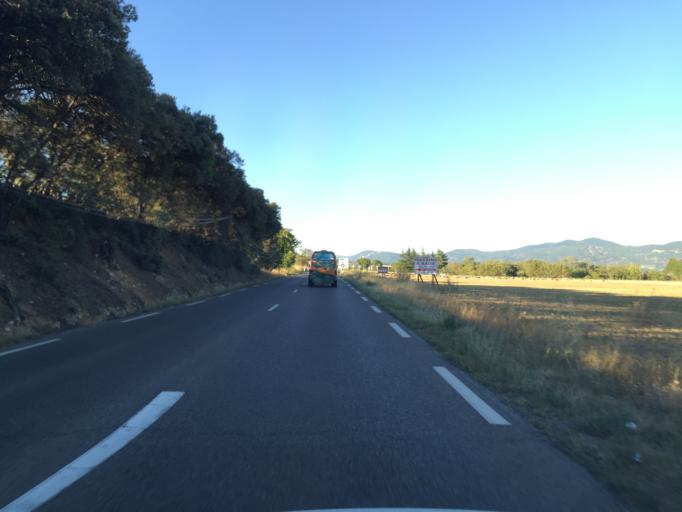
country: FR
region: Provence-Alpes-Cote d'Azur
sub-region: Departement des Alpes-de-Haute-Provence
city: Les Mees
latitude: 44.0494
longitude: 5.9614
